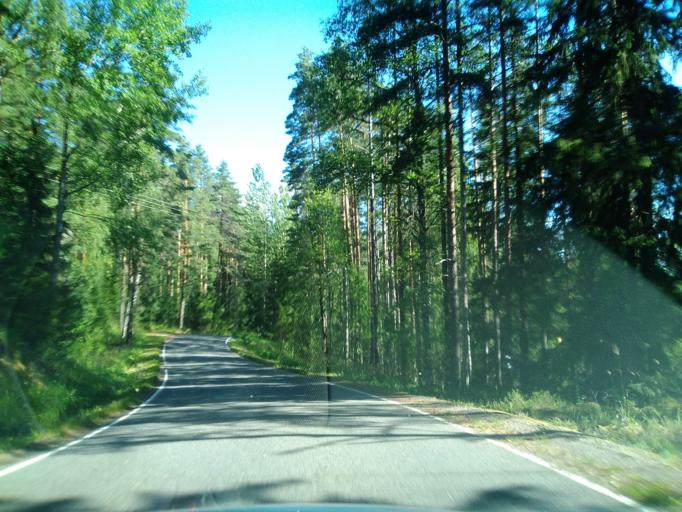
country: FI
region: Uusimaa
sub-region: Helsinki
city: Kaerkoelae
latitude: 60.7878
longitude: 24.0803
